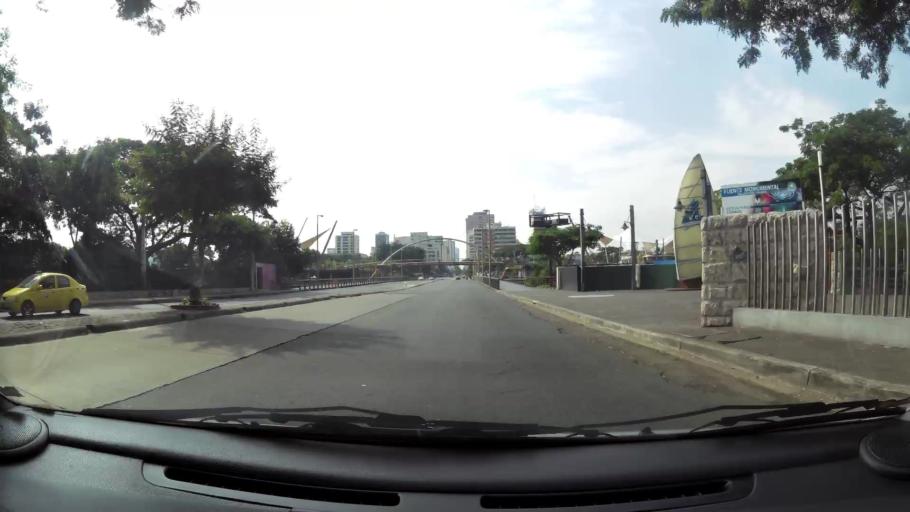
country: EC
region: Guayas
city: Guayaquil
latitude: -2.1862
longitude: -79.8991
